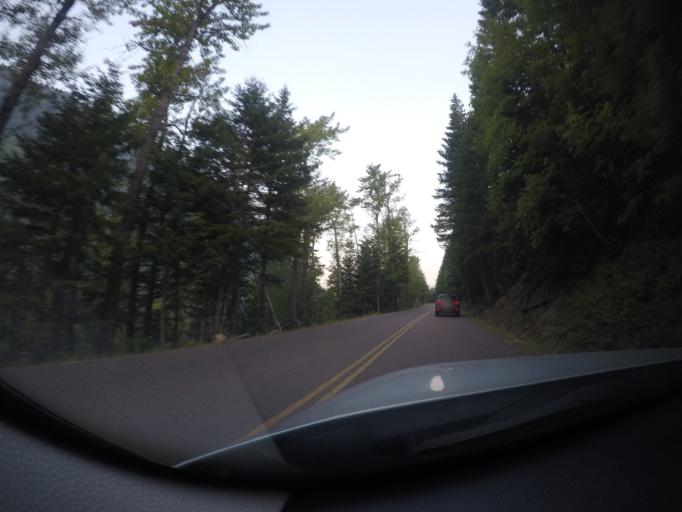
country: US
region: Montana
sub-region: Flathead County
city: Columbia Falls
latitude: 48.7367
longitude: -113.7655
